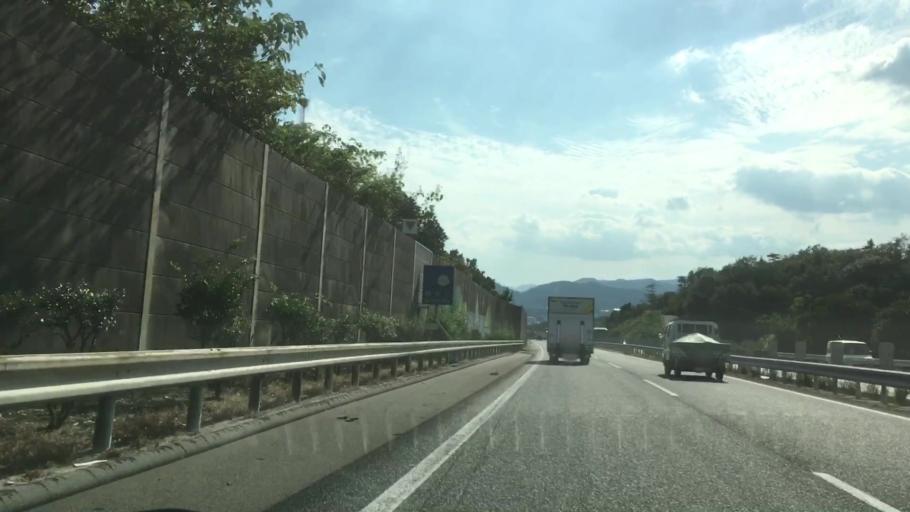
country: JP
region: Hiroshima
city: Ono-hara
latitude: 34.2700
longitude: 132.2445
